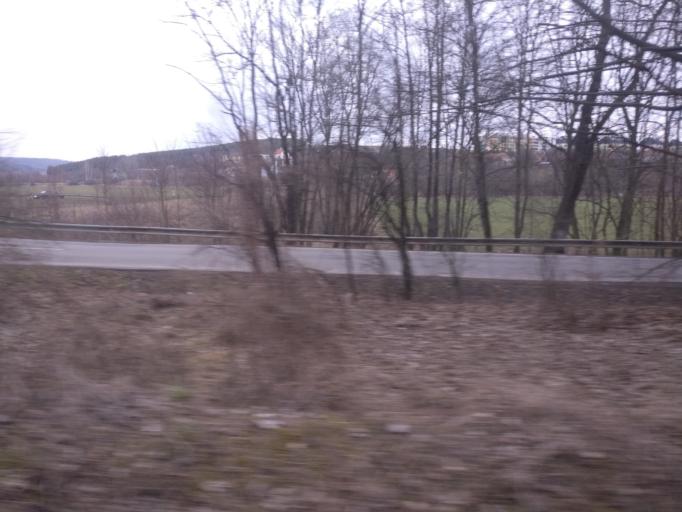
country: CZ
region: South Moravian
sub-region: Okres Brno-Venkov
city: Rosice
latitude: 49.1826
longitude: 16.3754
